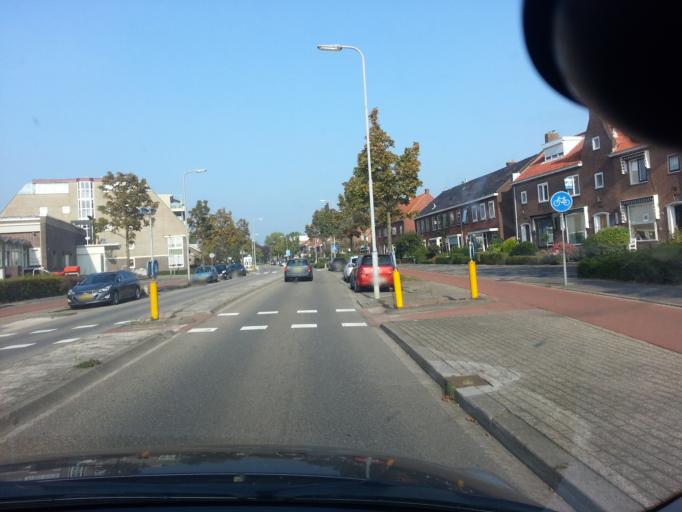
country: NL
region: South Holland
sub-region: Gemeente Zwijndrecht
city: Zwijndrecht
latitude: 51.8197
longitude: 4.6451
